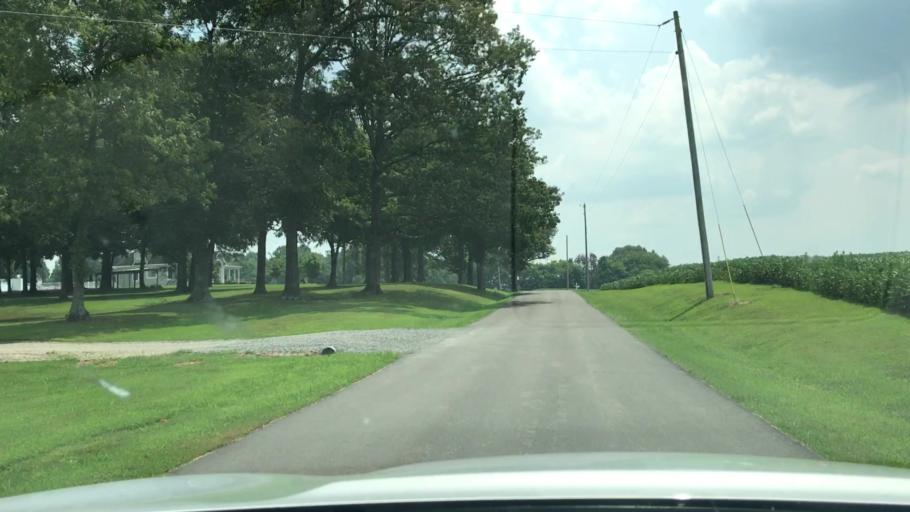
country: US
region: Kentucky
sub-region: Todd County
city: Elkton
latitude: 36.7676
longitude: -87.1401
